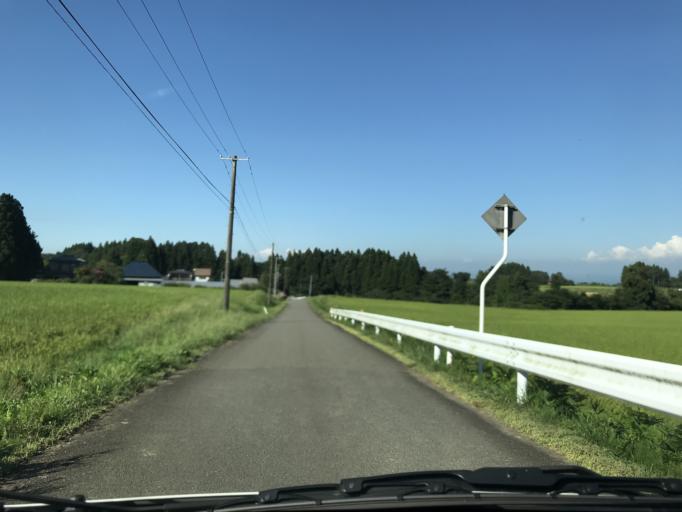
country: JP
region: Iwate
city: Mizusawa
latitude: 39.0691
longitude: 141.0452
